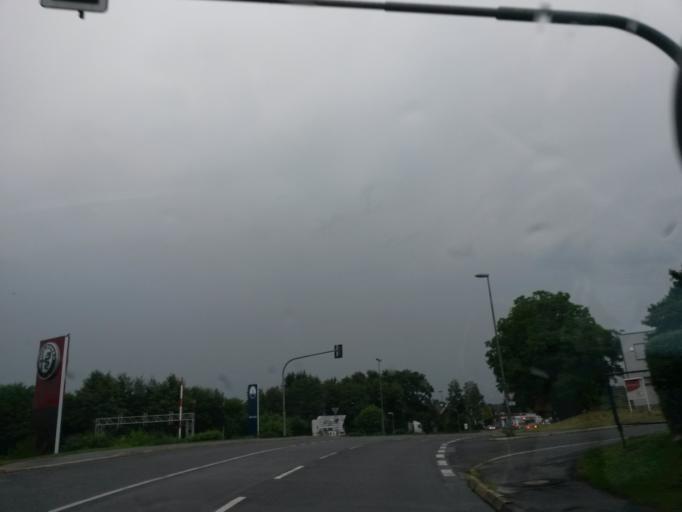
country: DE
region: North Rhine-Westphalia
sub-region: Regierungsbezirk Koln
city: Marienheide
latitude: 51.0527
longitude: 7.5432
